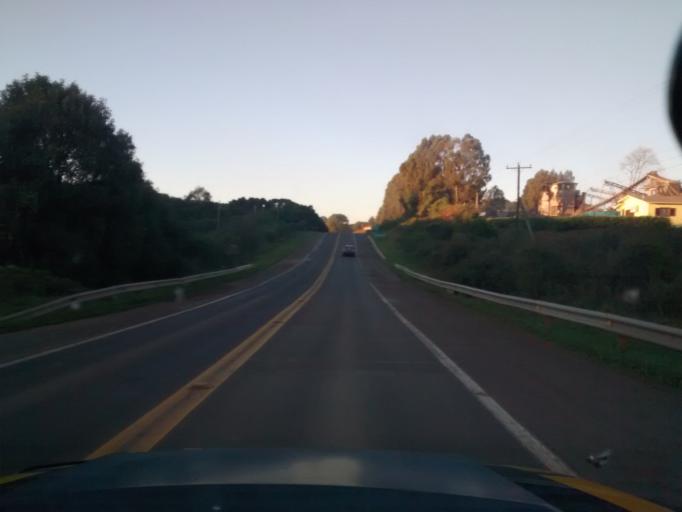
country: BR
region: Rio Grande do Sul
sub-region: Vacaria
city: Vacaria
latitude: -28.5346
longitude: -50.9585
